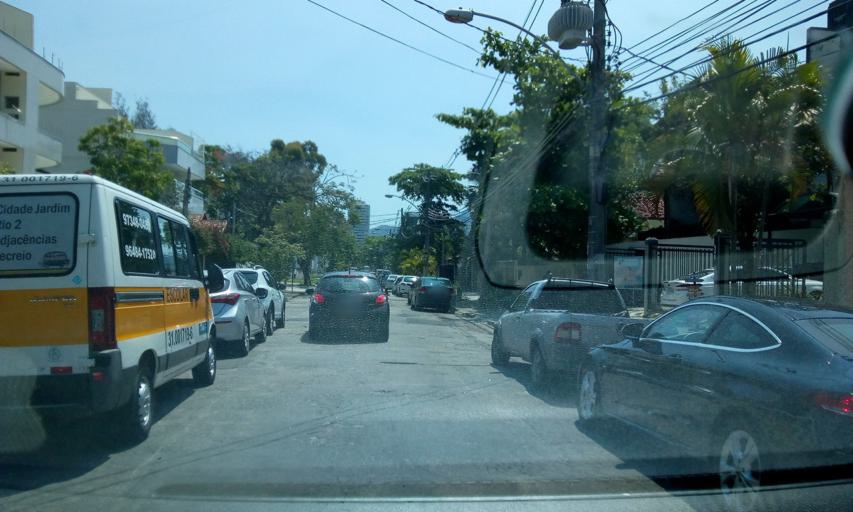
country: BR
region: Rio de Janeiro
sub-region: Nilopolis
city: Nilopolis
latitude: -23.0190
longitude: -43.4795
